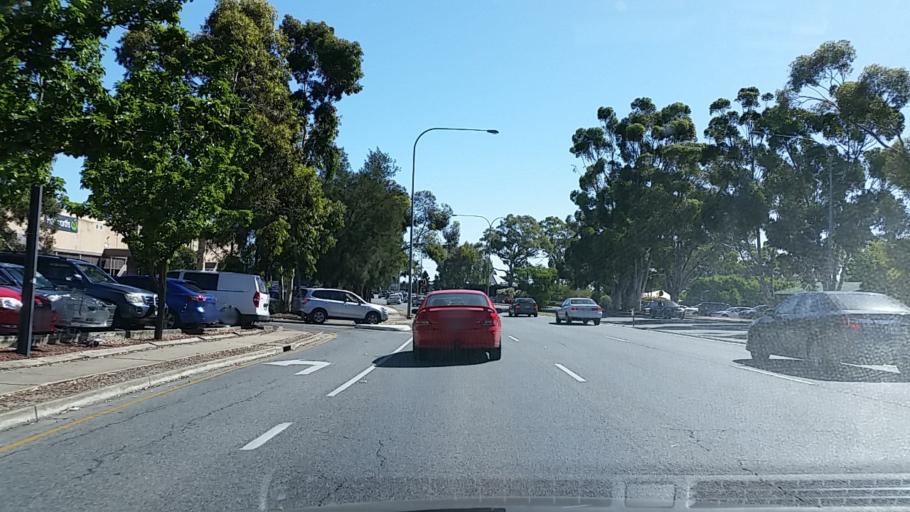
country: AU
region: South Australia
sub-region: Tea Tree Gully
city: Modbury
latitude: -34.8292
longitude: 138.6910
